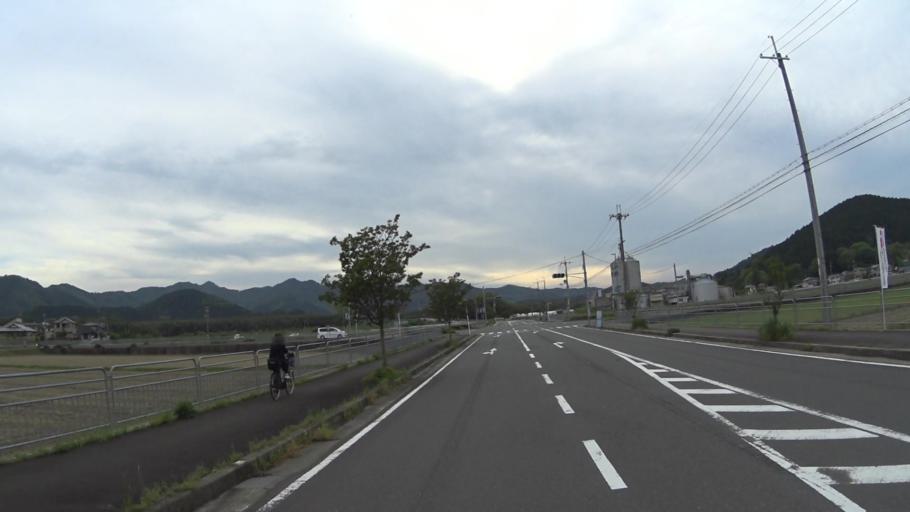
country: JP
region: Kyoto
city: Kameoka
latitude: 35.0772
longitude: 135.5375
